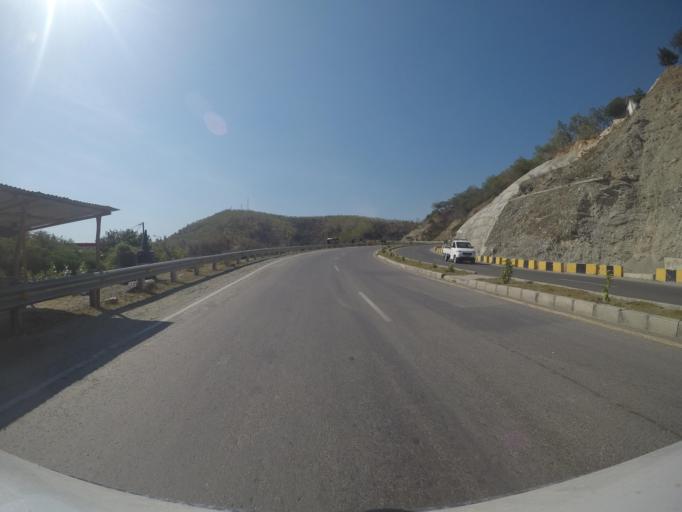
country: TL
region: Dili
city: Dili
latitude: -8.5672
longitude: 125.4910
